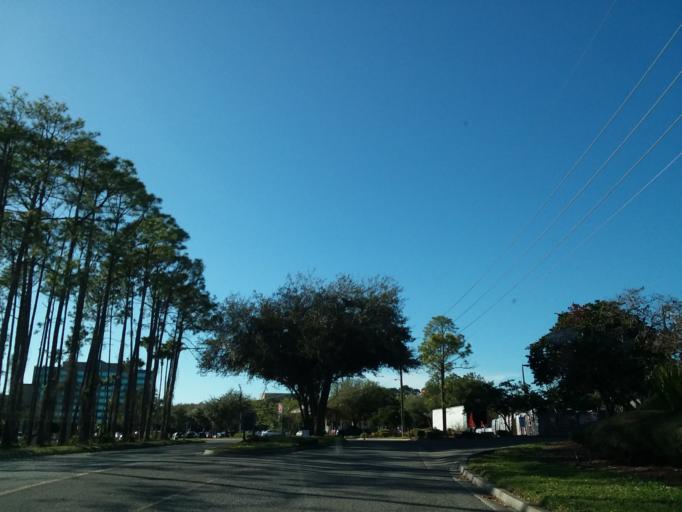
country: US
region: Florida
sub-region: Saint Johns County
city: Fruit Cove
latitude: 30.1950
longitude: -81.5495
